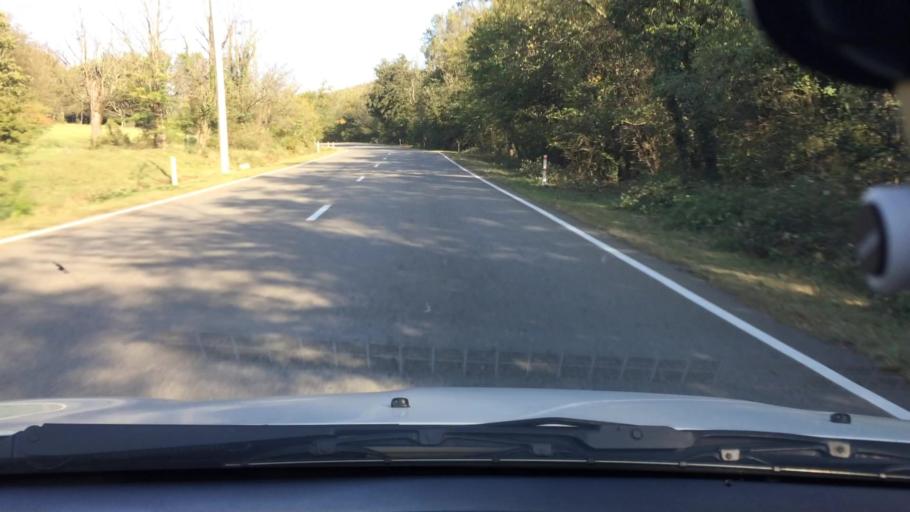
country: GE
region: Imereti
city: Kutaisi
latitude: 42.2489
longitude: 42.7552
